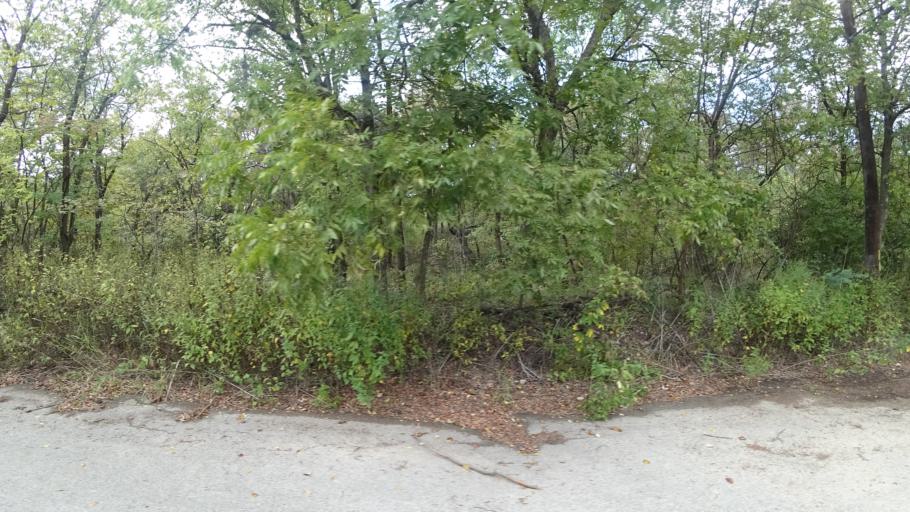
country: US
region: Texas
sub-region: Travis County
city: Austin
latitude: 30.2553
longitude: -97.7588
